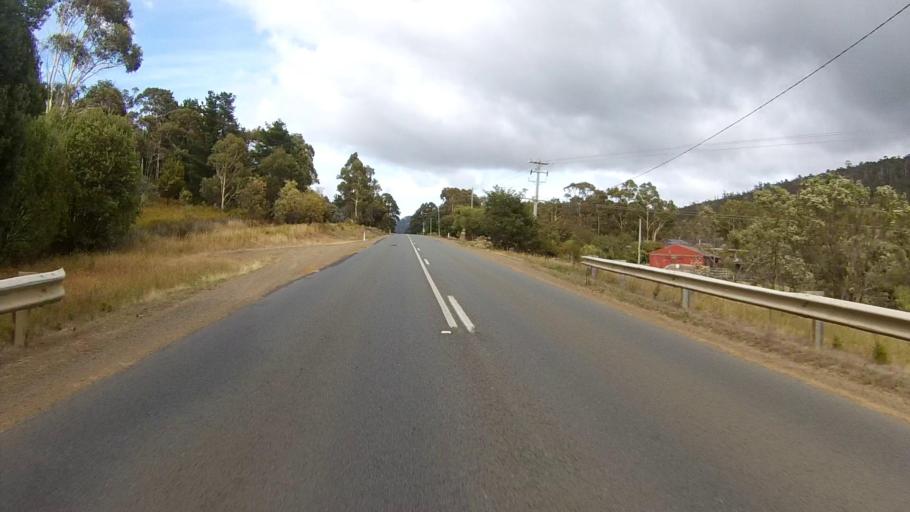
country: AU
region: Tasmania
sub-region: Kingborough
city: Kettering
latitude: -43.0919
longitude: 147.2478
